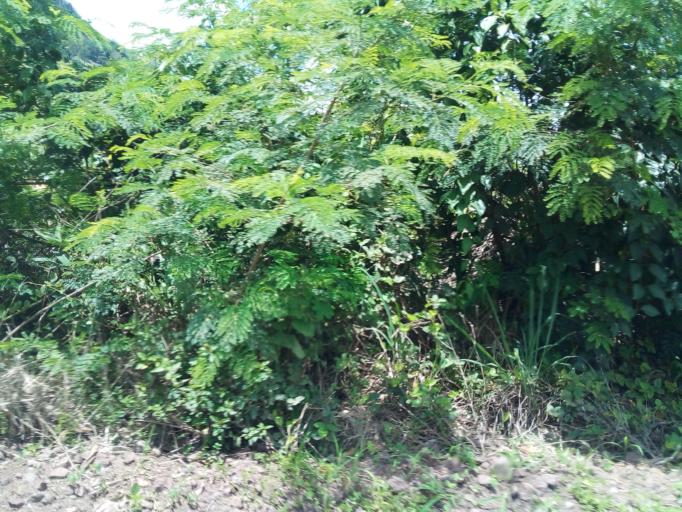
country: BR
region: Espirito Santo
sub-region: Fundao
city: Fundao
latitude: -19.9168
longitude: -40.3902
